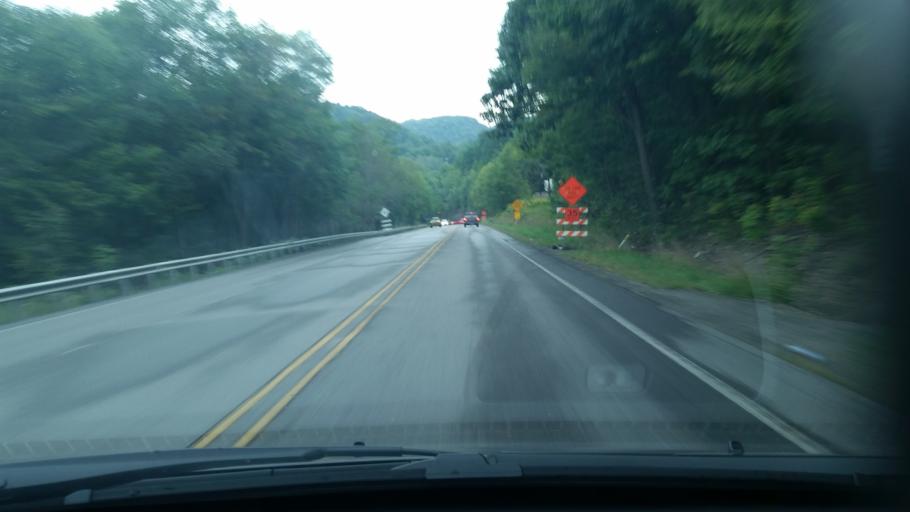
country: US
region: Pennsylvania
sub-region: Clearfield County
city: Shiloh
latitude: 41.0670
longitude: -78.3549
